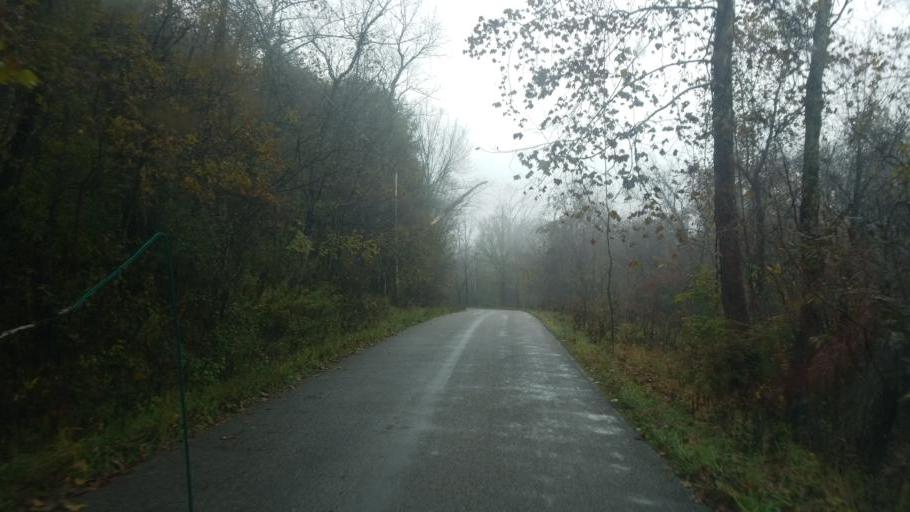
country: US
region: Ohio
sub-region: Athens County
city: Glouster
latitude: 39.4547
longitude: -81.9288
